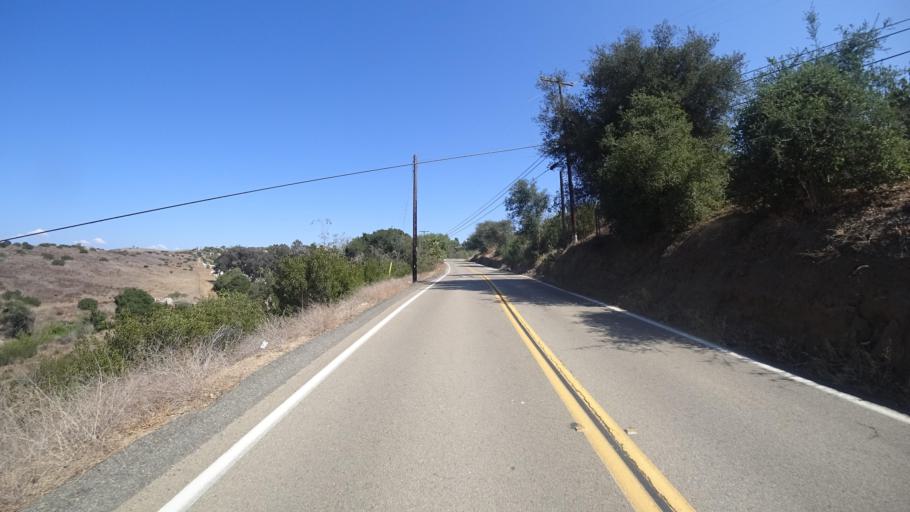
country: US
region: California
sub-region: San Diego County
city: Bonsall
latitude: 33.2968
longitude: -117.1983
